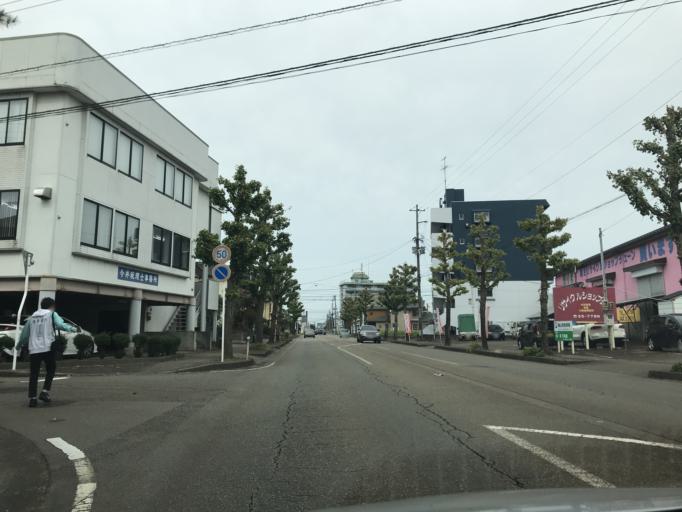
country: JP
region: Niigata
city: Nagaoka
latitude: 37.4307
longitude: 138.8373
